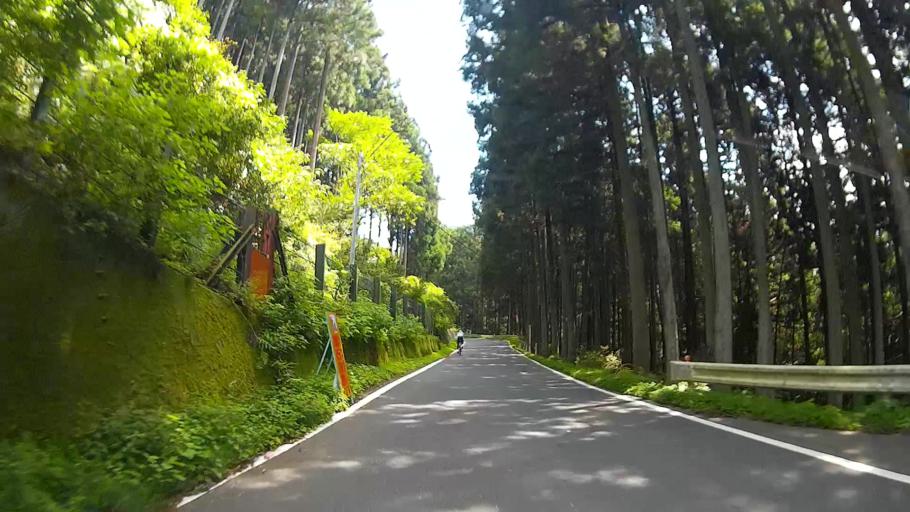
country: JP
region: Saitama
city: Chichibu
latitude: 35.9277
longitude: 139.1498
